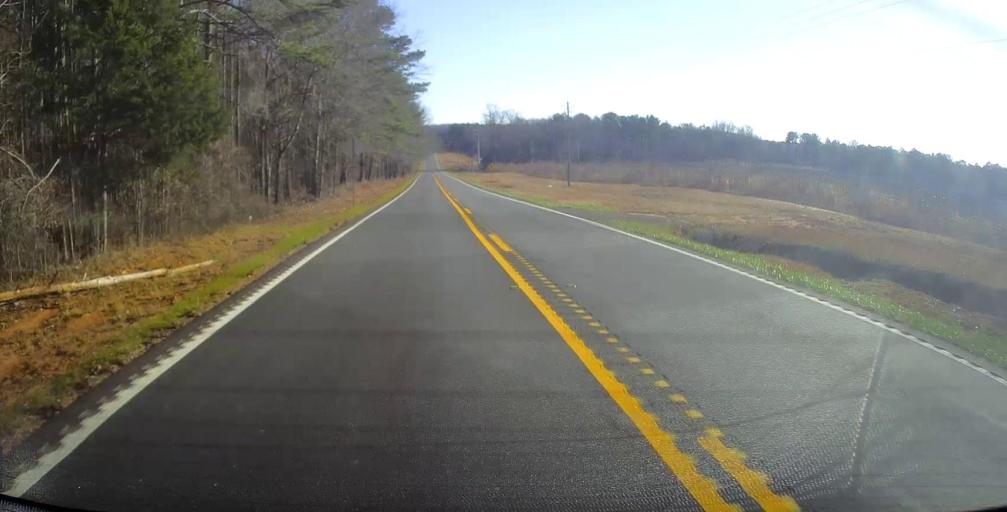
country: US
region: Georgia
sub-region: Talbot County
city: Sardis
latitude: 32.7961
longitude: -84.6928
